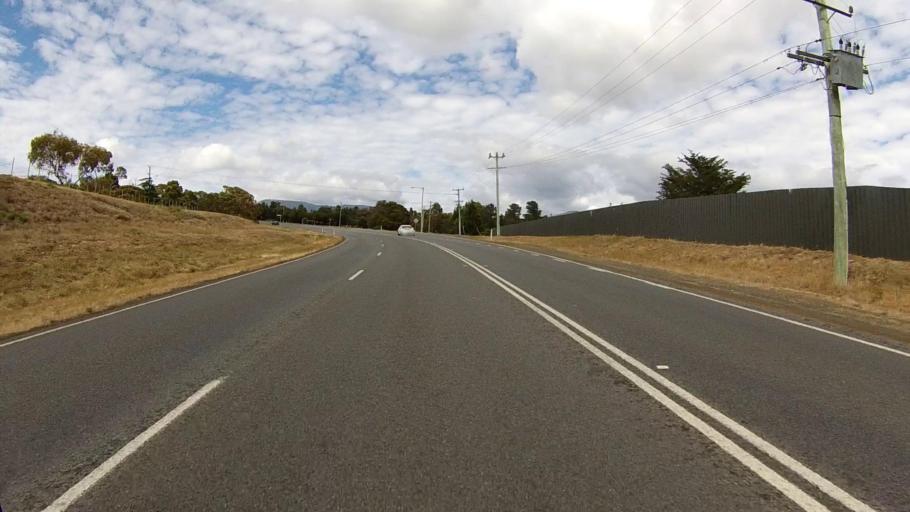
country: AU
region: Tasmania
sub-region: Brighton
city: Old Beach
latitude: -42.7960
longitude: 147.2906
